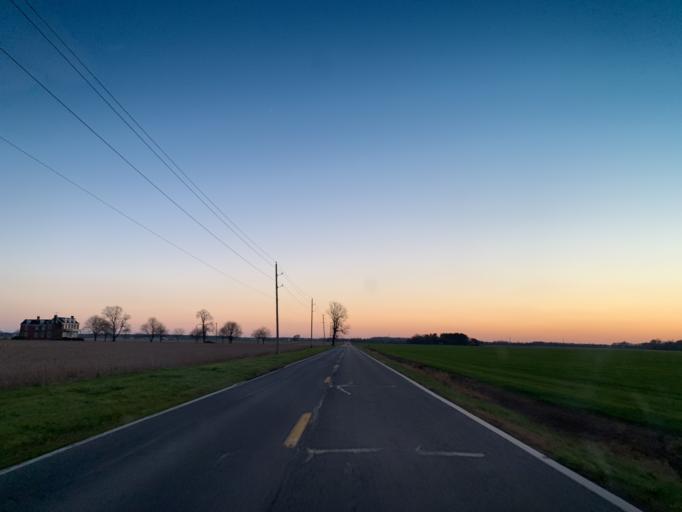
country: US
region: Delaware
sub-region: New Castle County
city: Middletown
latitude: 39.4177
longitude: -75.7441
